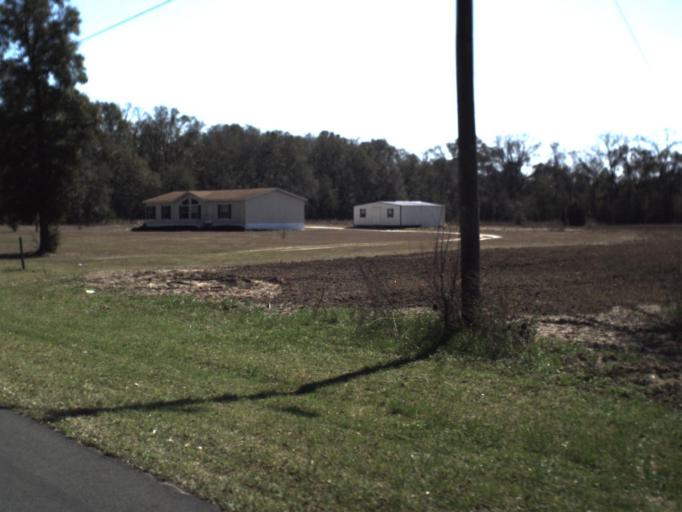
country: US
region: Florida
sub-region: Jackson County
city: Malone
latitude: 30.8648
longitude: -85.1169
